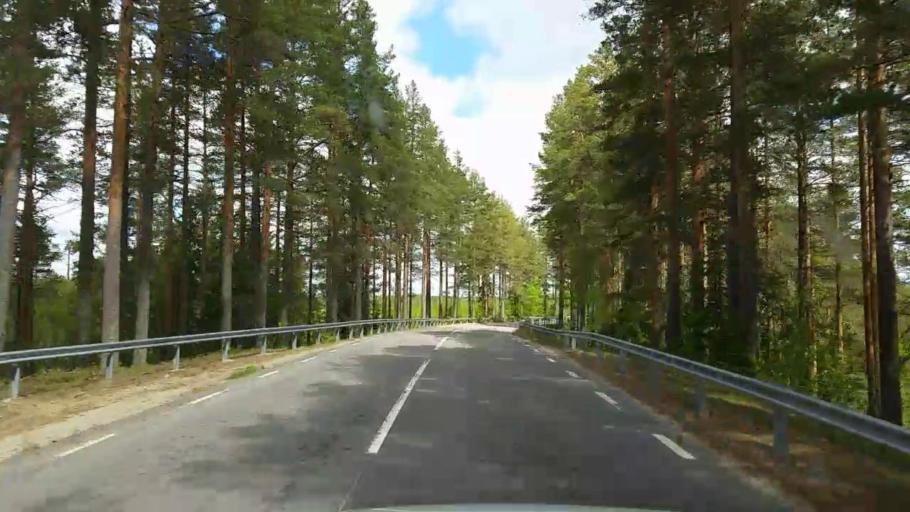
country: SE
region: Gaevleborg
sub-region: Bollnas Kommun
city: Vittsjo
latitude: 61.1209
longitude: 16.1628
